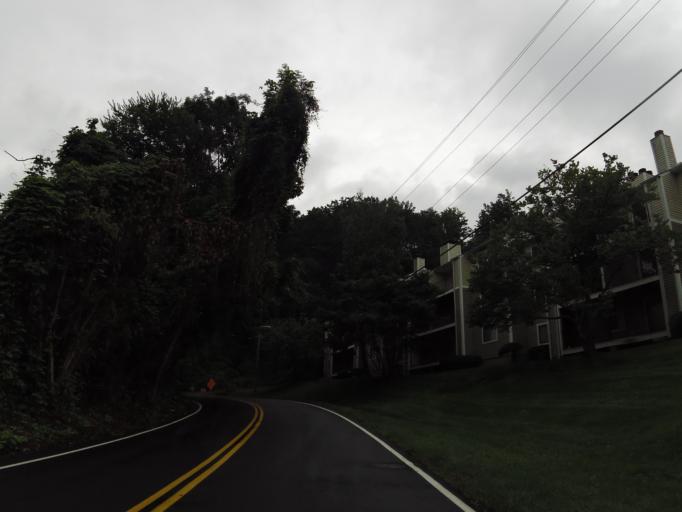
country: US
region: Tennessee
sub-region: Knox County
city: Knoxville
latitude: 35.9486
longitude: -83.9093
